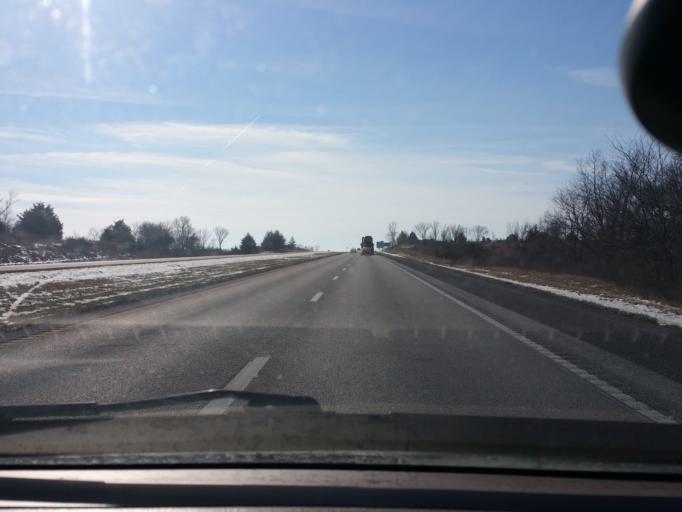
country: US
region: Missouri
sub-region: Clinton County
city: Cameron
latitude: 39.8633
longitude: -94.1726
